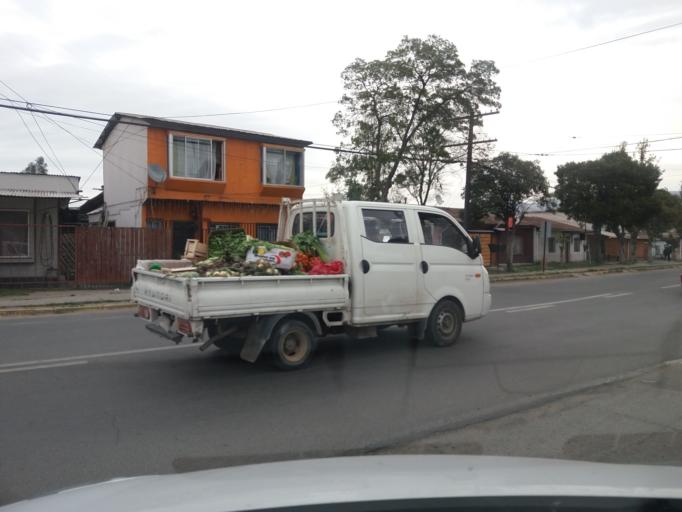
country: CL
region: Valparaiso
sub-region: Provincia de Quillota
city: Hacienda La Calera
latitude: -32.7790
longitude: -71.1852
